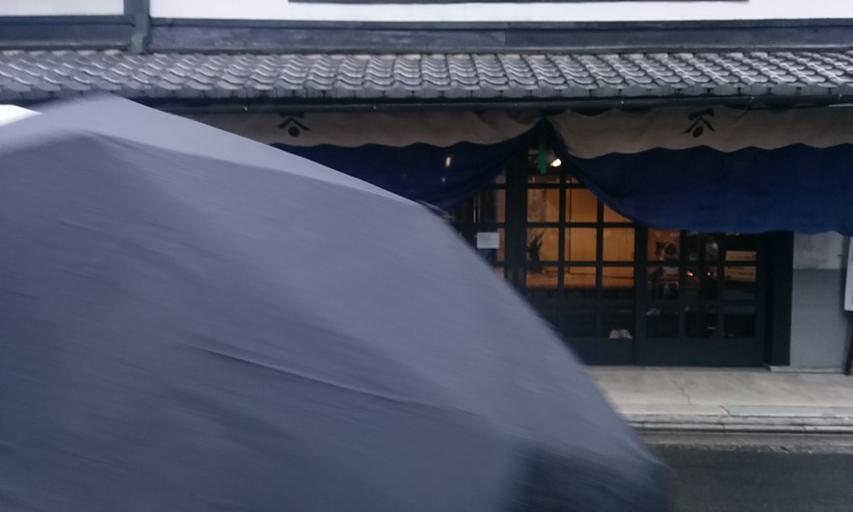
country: JP
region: Kyoto
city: Kyoto
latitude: 35.0009
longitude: 135.7582
